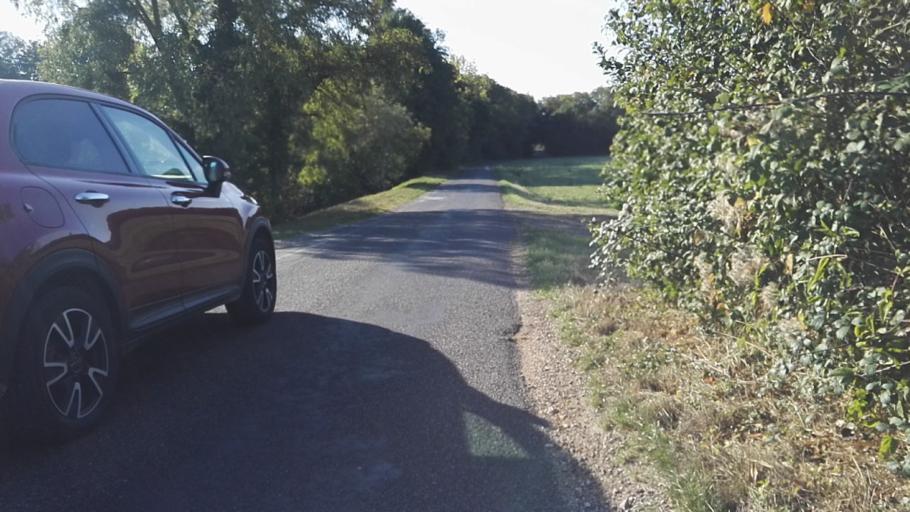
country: FR
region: Haute-Normandie
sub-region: Departement de l'Eure
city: Menilles
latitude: 49.0521
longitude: 1.3363
